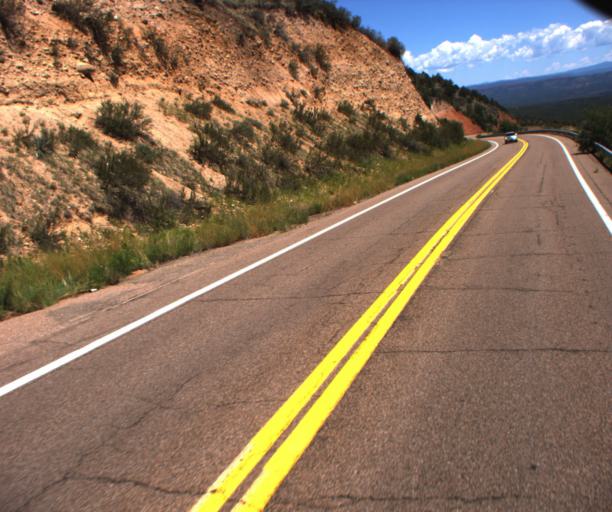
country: US
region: Arizona
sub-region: Navajo County
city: Cibecue
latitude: 33.9294
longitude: -110.3569
